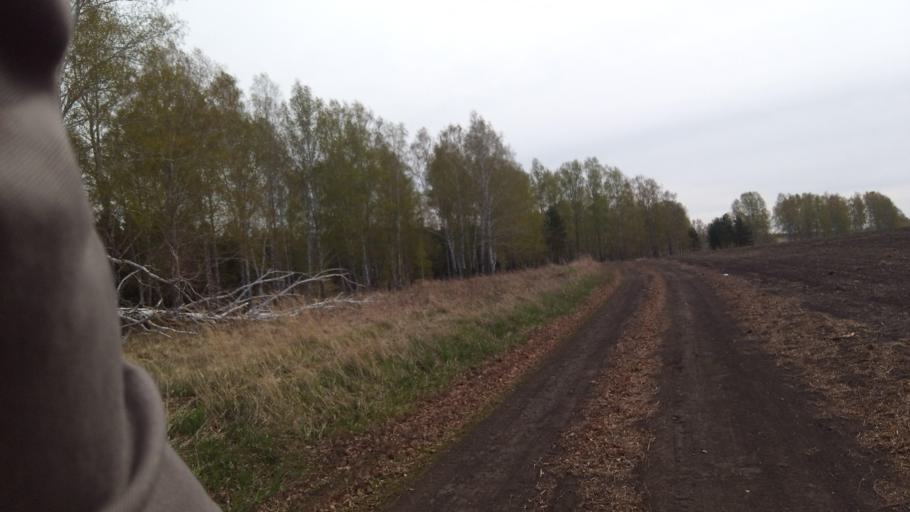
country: RU
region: Chelyabinsk
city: Timiryazevskiy
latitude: 55.0187
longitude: 60.8545
